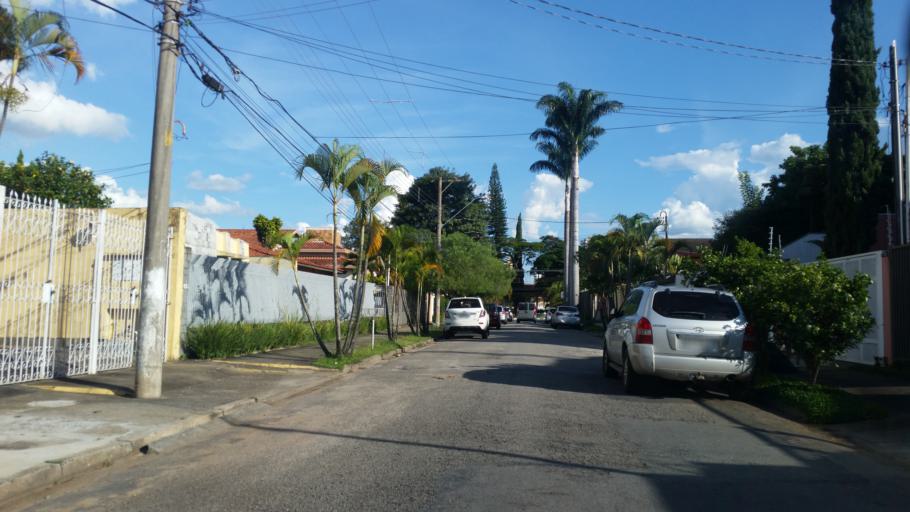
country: BR
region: Sao Paulo
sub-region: Taubate
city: Taubate
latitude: -23.0290
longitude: -45.5720
